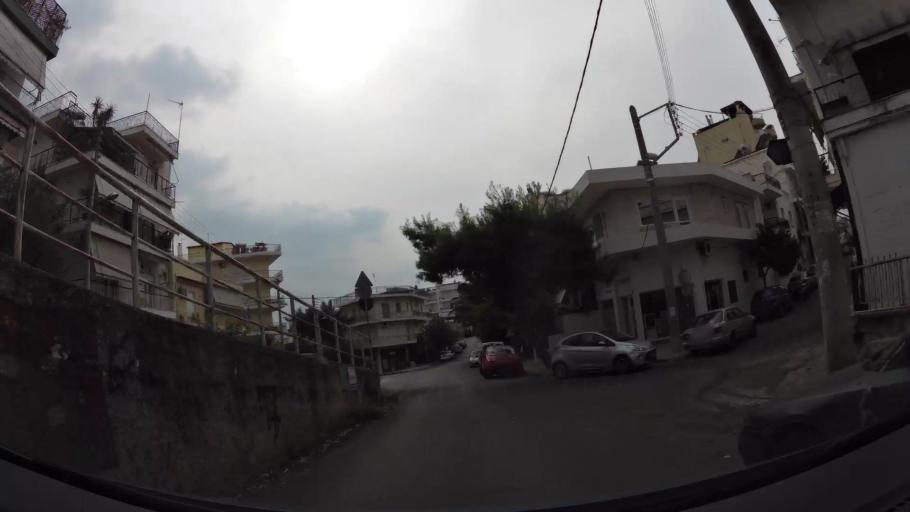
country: GR
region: Attica
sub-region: Nomarchia Athinas
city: Agios Dimitrios
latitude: 37.9208
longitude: 23.7341
